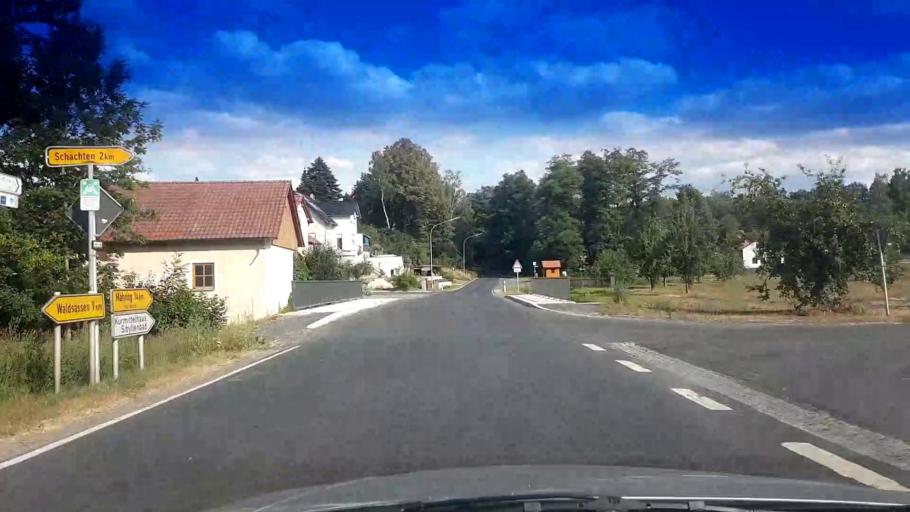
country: DE
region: Bavaria
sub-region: Upper Palatinate
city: Neualbenreuth
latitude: 49.9887
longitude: 12.4087
